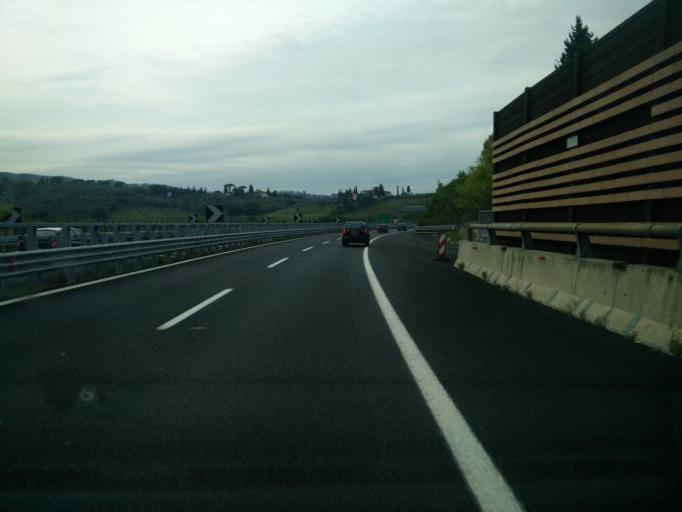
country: IT
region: Tuscany
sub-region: Province of Florence
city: Scandicci
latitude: 43.7314
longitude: 11.1911
